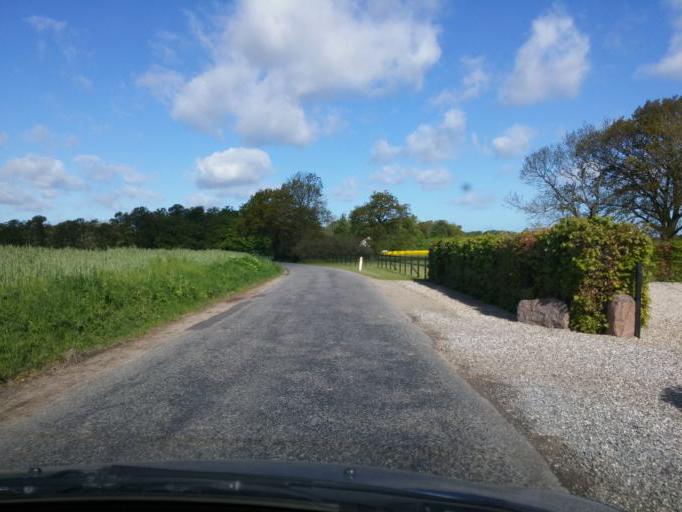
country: DK
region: South Denmark
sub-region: Kerteminde Kommune
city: Munkebo
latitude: 55.4128
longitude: 10.5396
